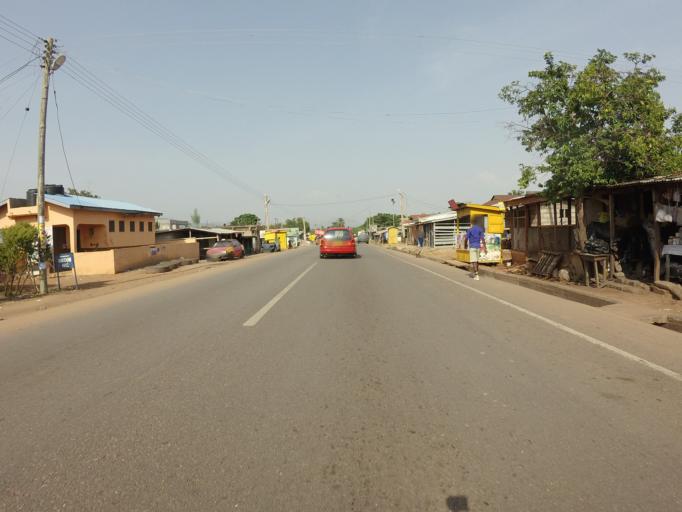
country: GH
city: Akropong
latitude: 6.1111
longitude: -0.0075
